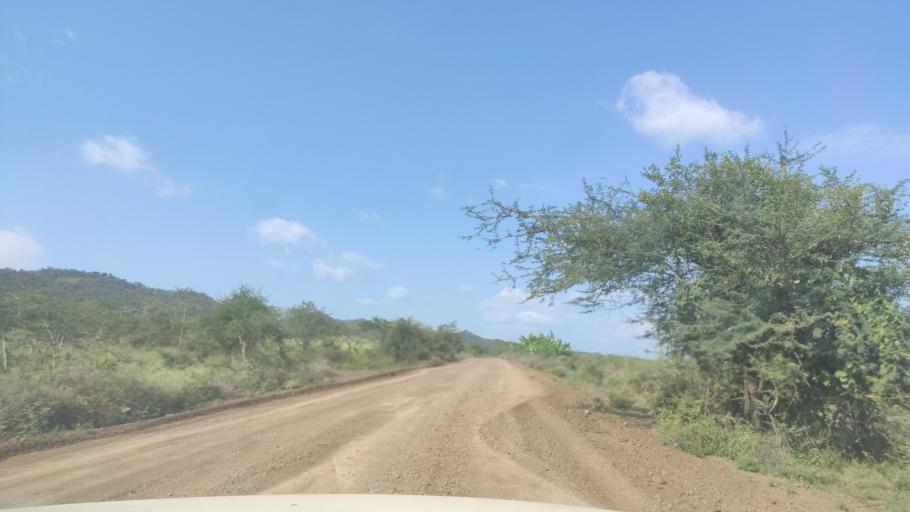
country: ET
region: Southern Nations, Nationalities, and People's Region
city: Felege Neway
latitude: 6.3916
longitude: 37.0992
